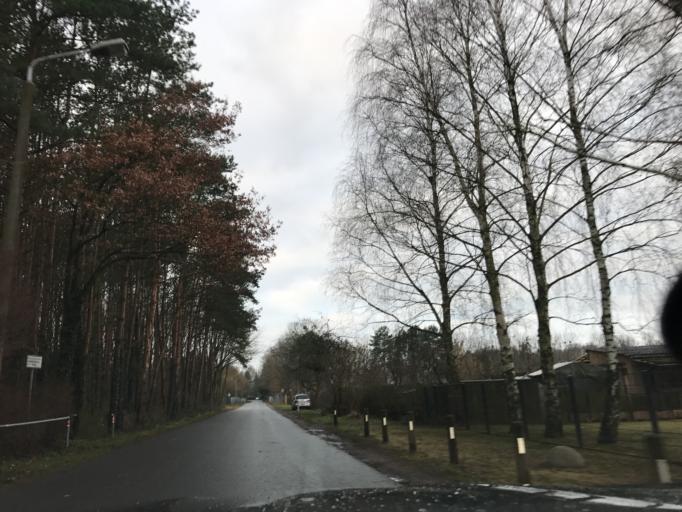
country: DE
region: Brandenburg
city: Potsdam
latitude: 52.4379
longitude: 13.0319
